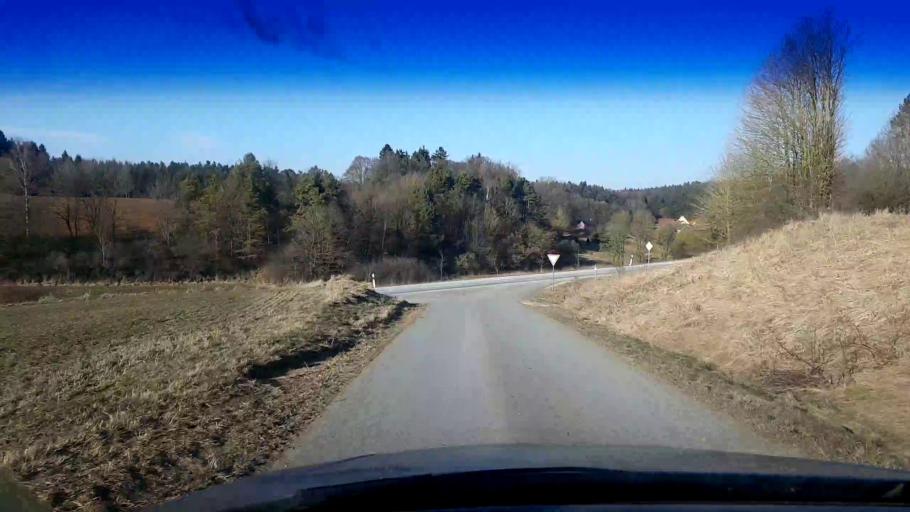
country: DE
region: Bavaria
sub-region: Upper Franconia
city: Aufsess
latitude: 49.9266
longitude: 11.2006
